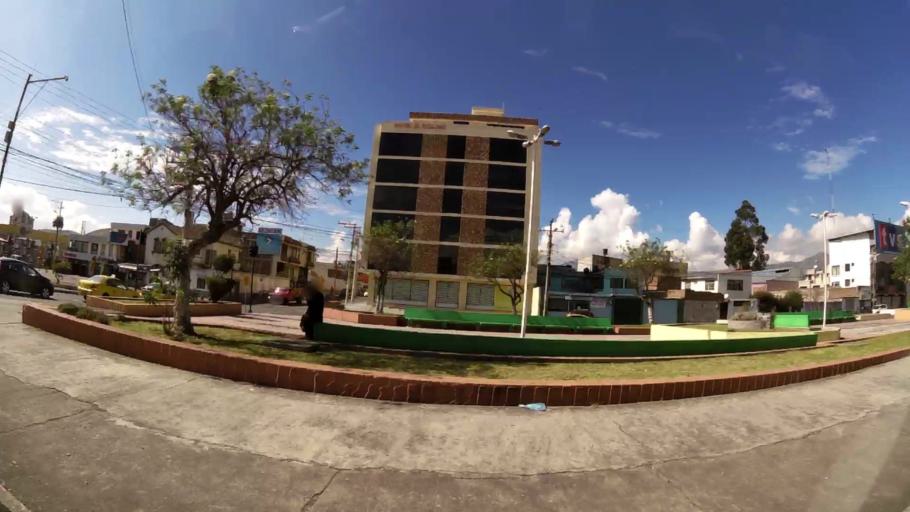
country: EC
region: Chimborazo
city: Riobamba
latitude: -1.6671
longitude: -78.6621
